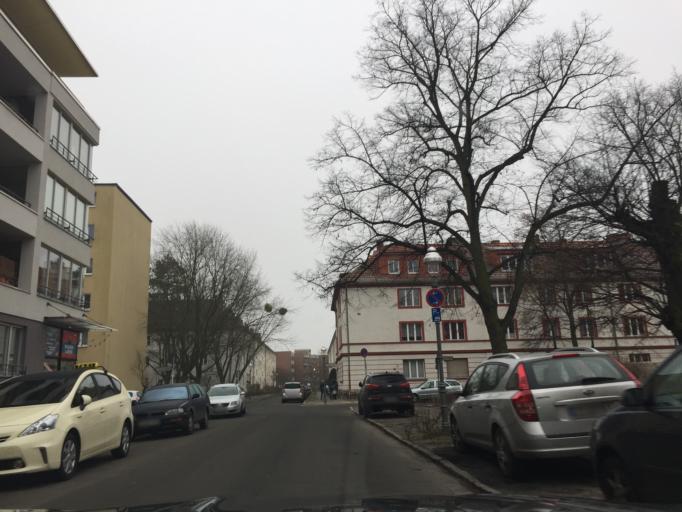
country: DE
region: Berlin
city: Wilhelmstadt
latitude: 52.5198
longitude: 13.1939
